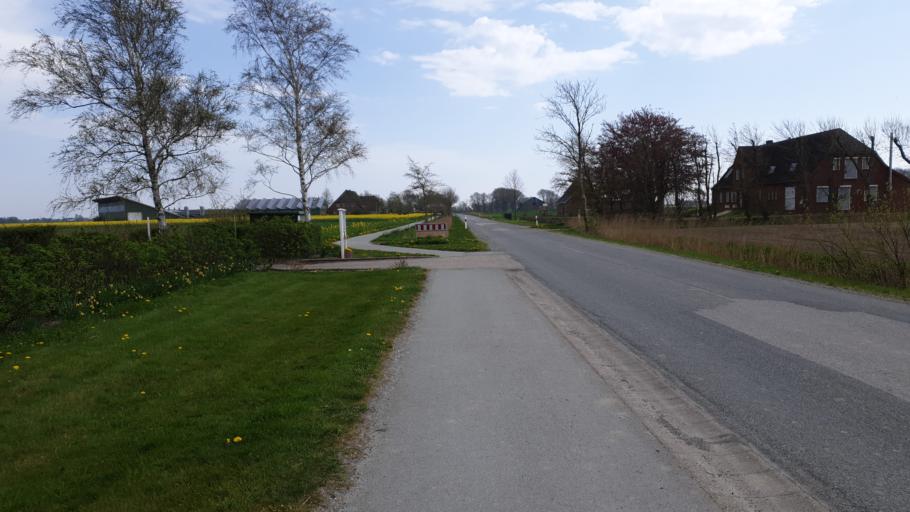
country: DE
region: Schleswig-Holstein
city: Elisabeth-Sophien-Koog
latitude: 54.4758
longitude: 8.8745
